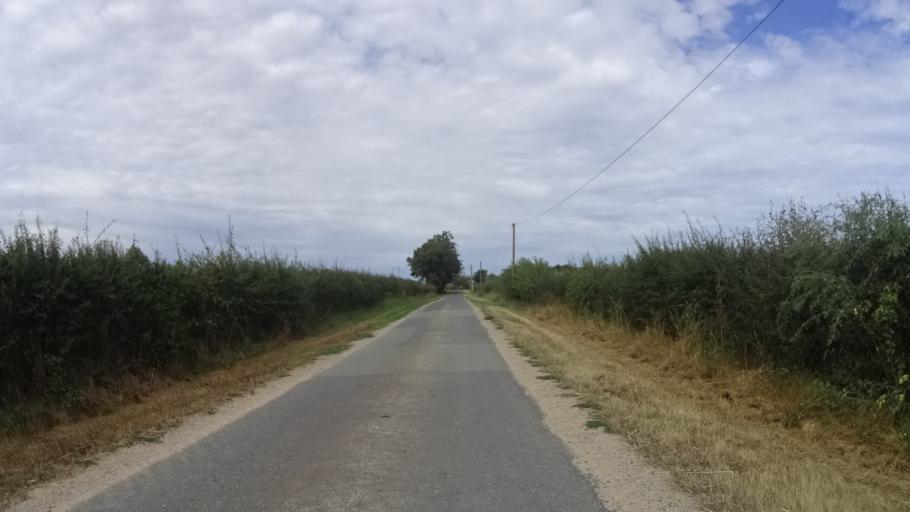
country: FR
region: Auvergne
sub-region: Departement de l'Allier
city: Beaulon
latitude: 46.6536
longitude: 3.6654
